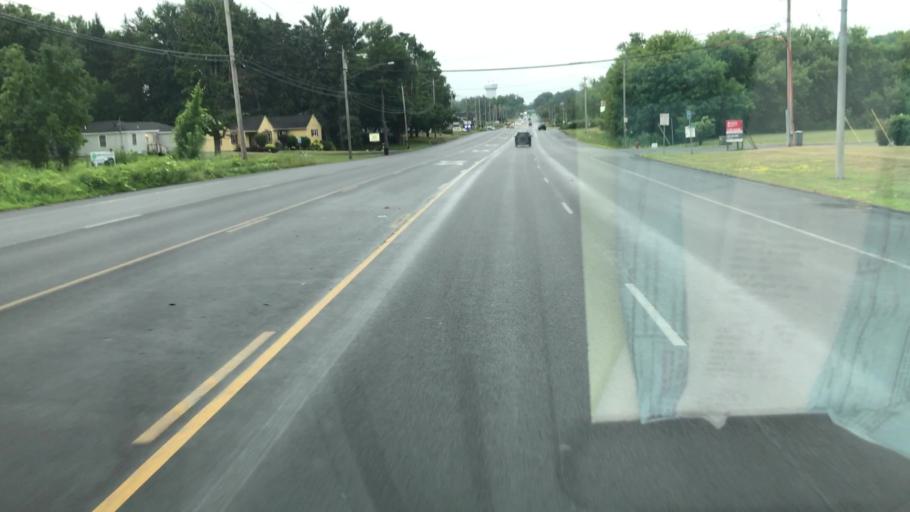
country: US
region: New York
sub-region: Onondaga County
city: Liverpool
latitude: 43.1241
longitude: -76.2170
